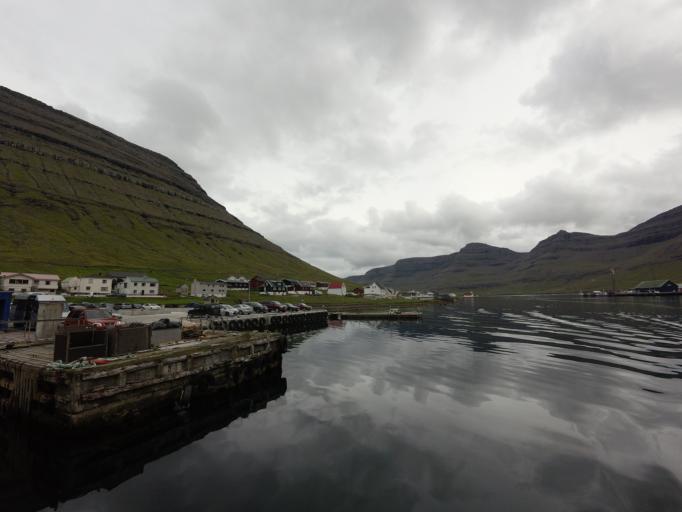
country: FO
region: Nordoyar
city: Klaksvik
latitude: 62.2978
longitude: -6.5227
